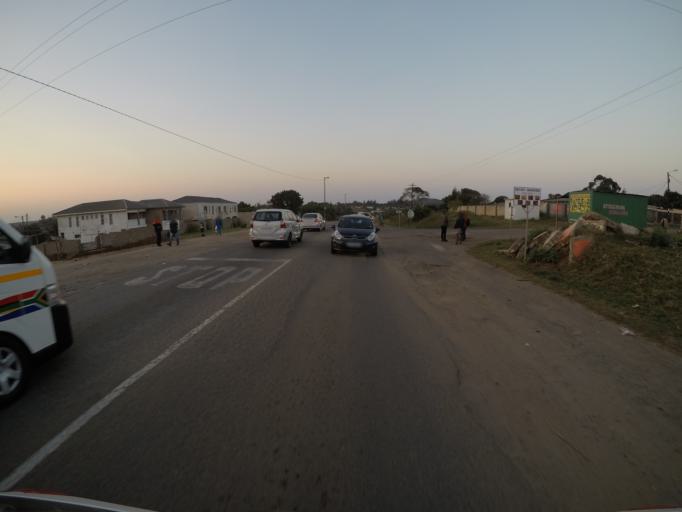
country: ZA
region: KwaZulu-Natal
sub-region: uThungulu District Municipality
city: Richards Bay
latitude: -28.7583
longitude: 32.1335
